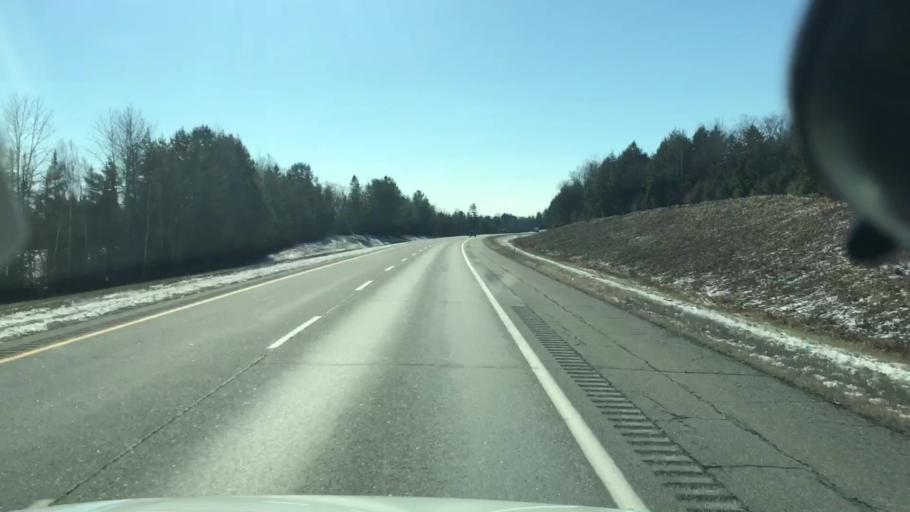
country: US
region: Maine
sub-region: Penobscot County
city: Howland
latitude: 45.2916
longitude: -68.6655
